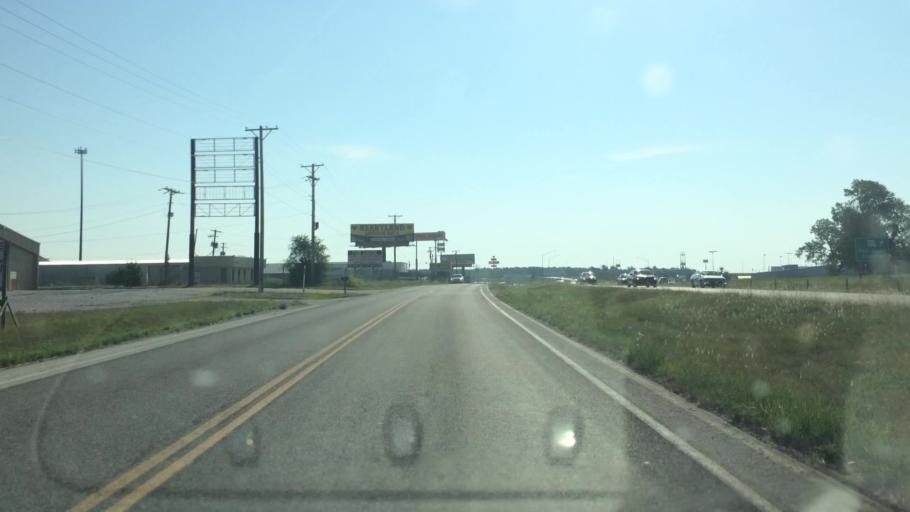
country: US
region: Missouri
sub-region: Greene County
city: Strafford
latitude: 37.2726
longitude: -93.1221
